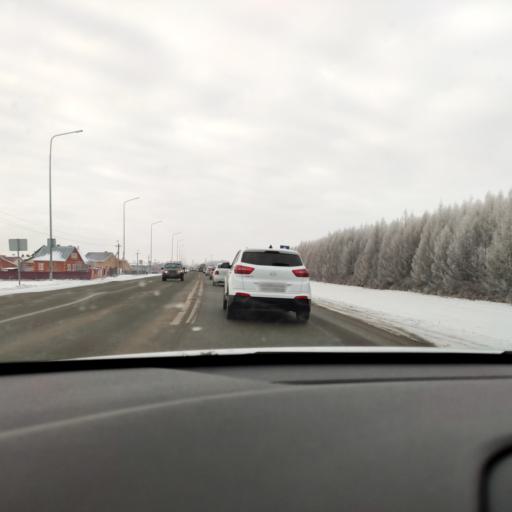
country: RU
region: Tatarstan
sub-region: Arskiy Rayon
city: Arsk
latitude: 56.1065
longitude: 49.8951
